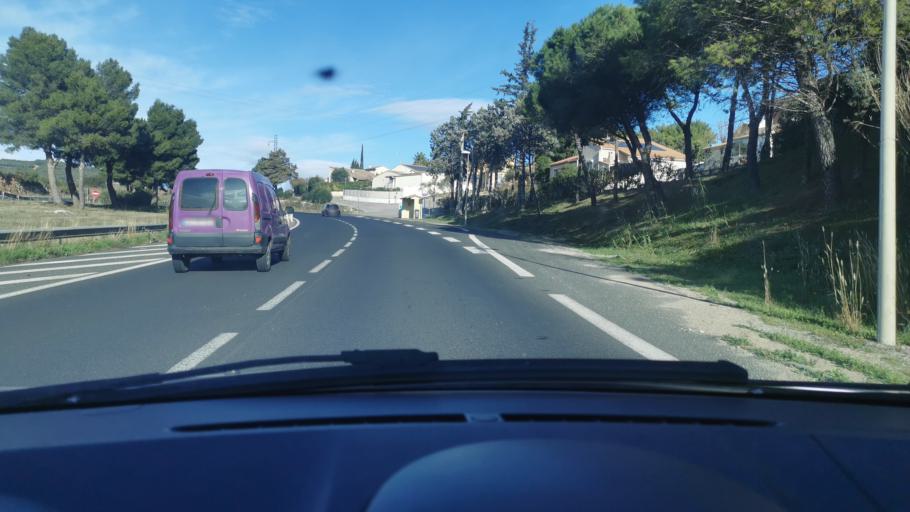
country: FR
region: Languedoc-Roussillon
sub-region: Departement de l'Herault
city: Mireval
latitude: 43.5172
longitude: 3.8082
